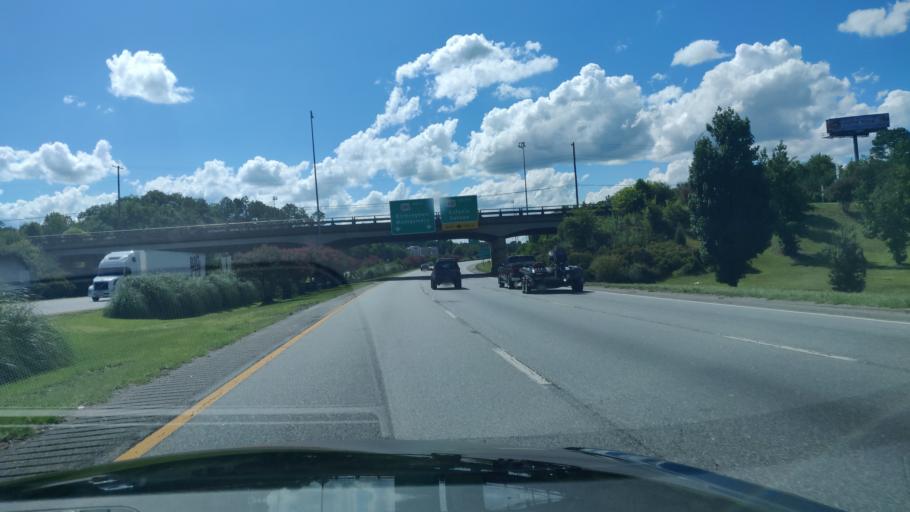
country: US
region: Alabama
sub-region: Russell County
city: Phenix City
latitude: 32.4533
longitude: -85.0047
